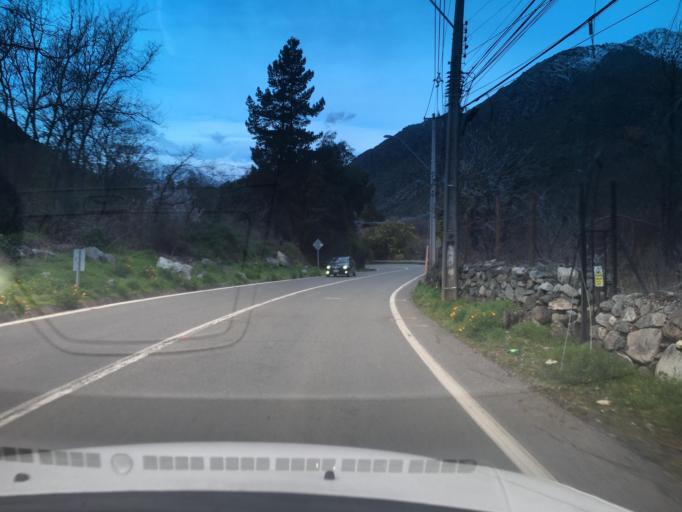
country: CL
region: Santiago Metropolitan
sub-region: Provincia de Cordillera
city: Puente Alto
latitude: -33.5758
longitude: -70.4442
